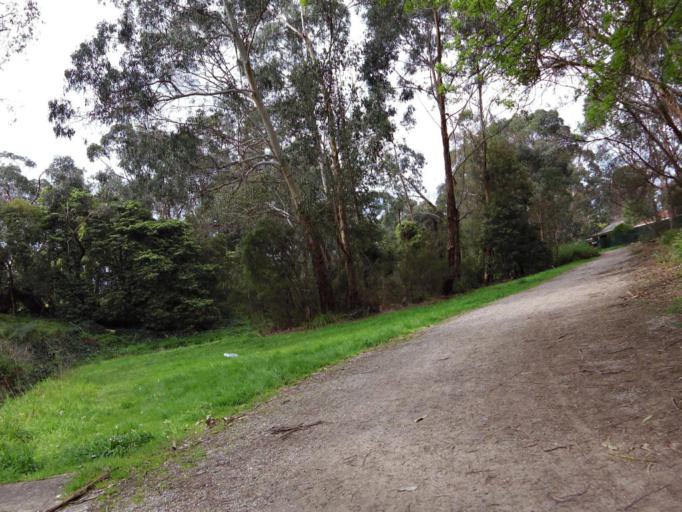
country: AU
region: Victoria
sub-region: Maroondah
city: Ringwood East
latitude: -37.8043
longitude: 145.2400
